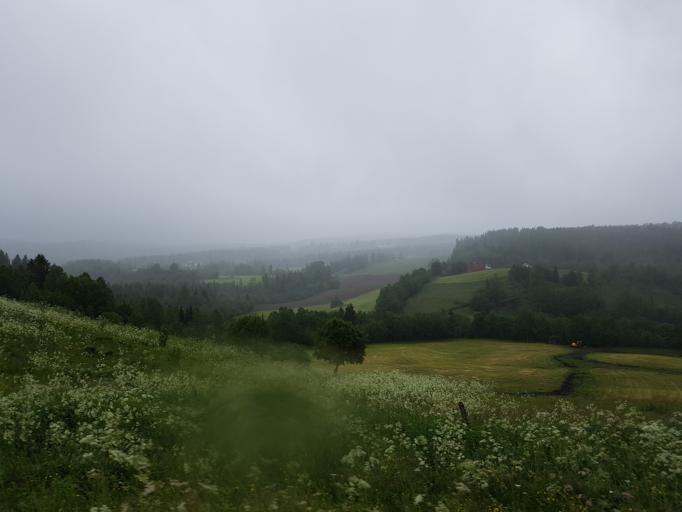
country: NO
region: Sor-Trondelag
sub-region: Selbu
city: Mebonden
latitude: 63.3856
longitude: 11.0778
